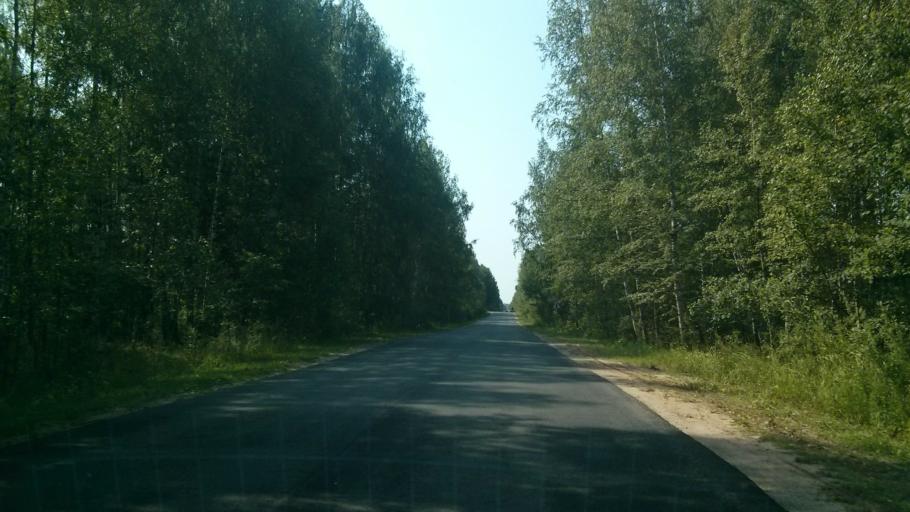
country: RU
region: Vladimir
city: Murom
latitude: 55.5189
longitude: 42.0201
